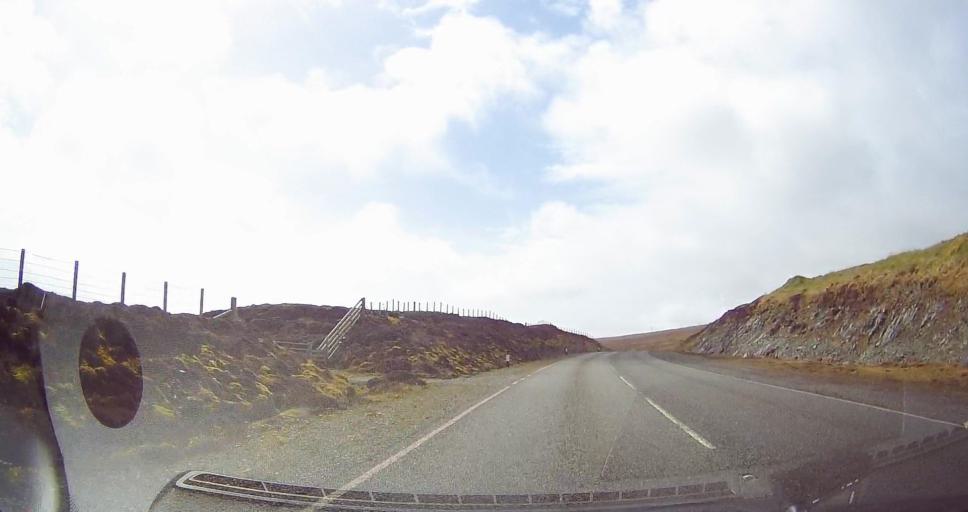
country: GB
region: Scotland
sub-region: Shetland Islands
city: Sandwick
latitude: 60.0897
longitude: -1.2285
